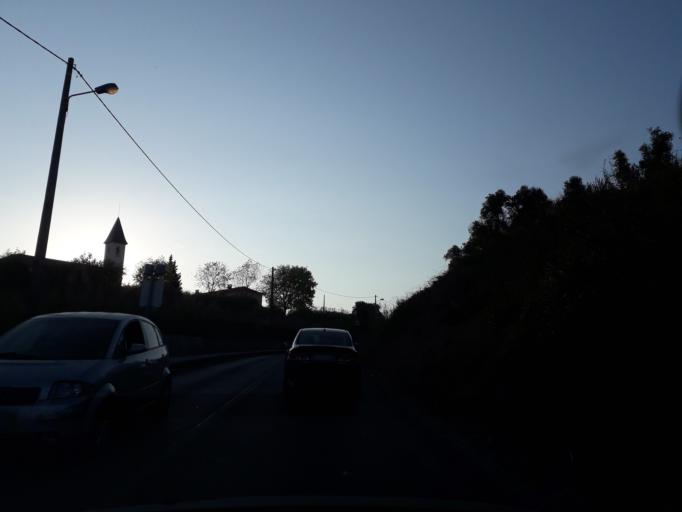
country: PT
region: Lisbon
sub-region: Odivelas
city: Pontinha
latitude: 38.7698
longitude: -9.1998
